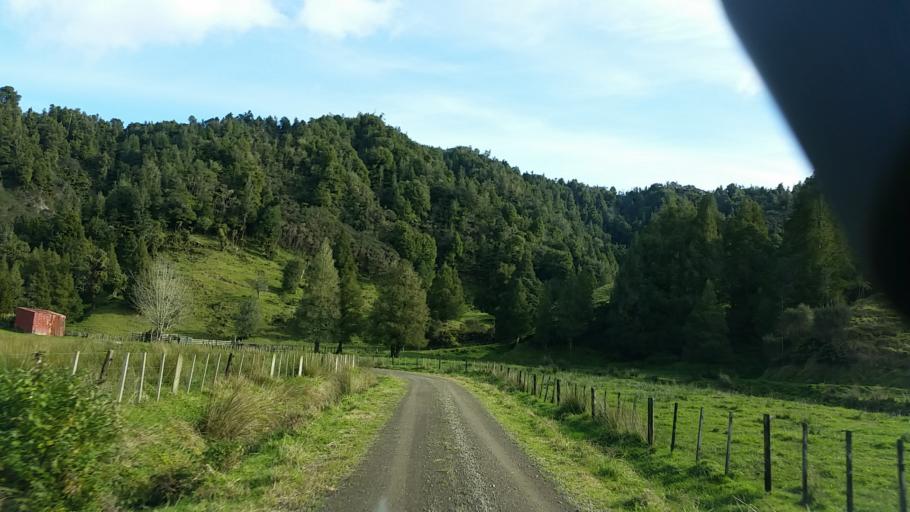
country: NZ
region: Taranaki
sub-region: New Plymouth District
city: Waitara
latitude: -39.0900
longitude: 174.4398
